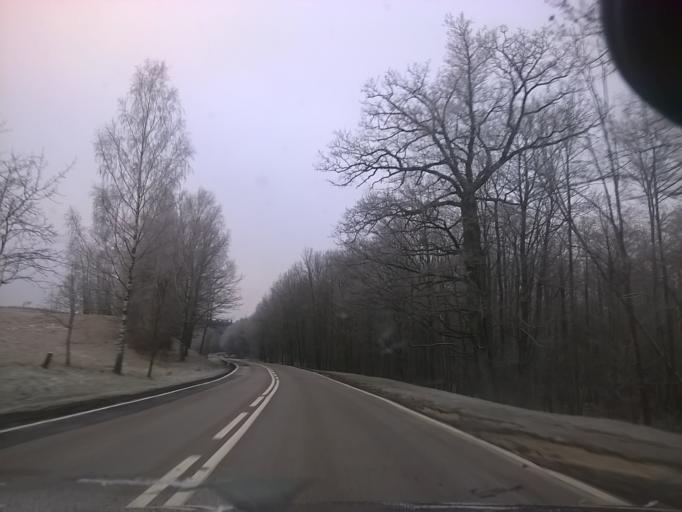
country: PL
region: Warmian-Masurian Voivodeship
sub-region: Powiat olsztynski
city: Biskupiec
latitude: 53.8422
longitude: 21.1222
